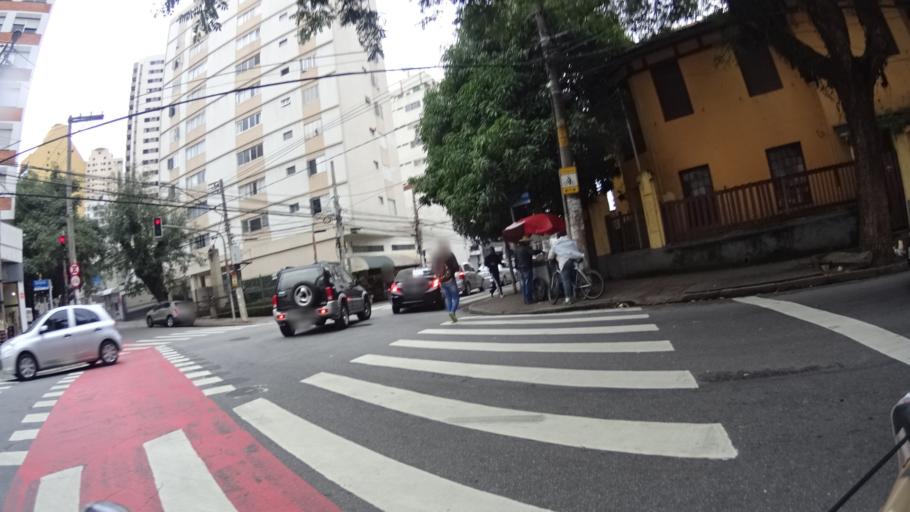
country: BR
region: Sao Paulo
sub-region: Sao Paulo
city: Sao Paulo
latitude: -23.5329
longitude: -46.6691
